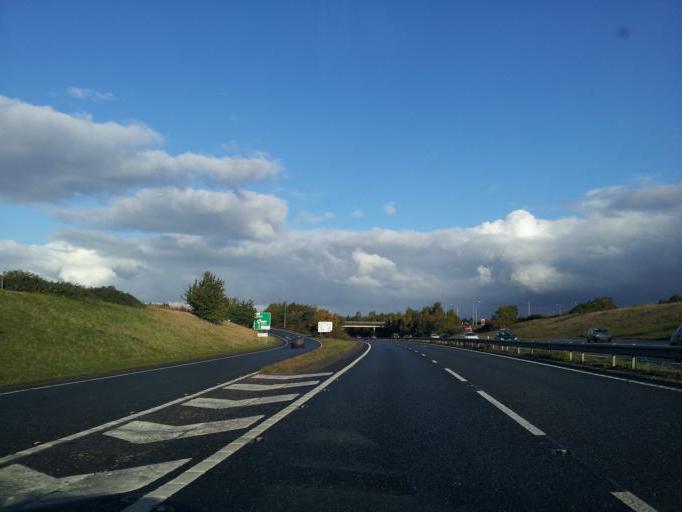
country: GB
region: England
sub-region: Norfolk
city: Costessey
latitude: 52.6482
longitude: 1.1878
